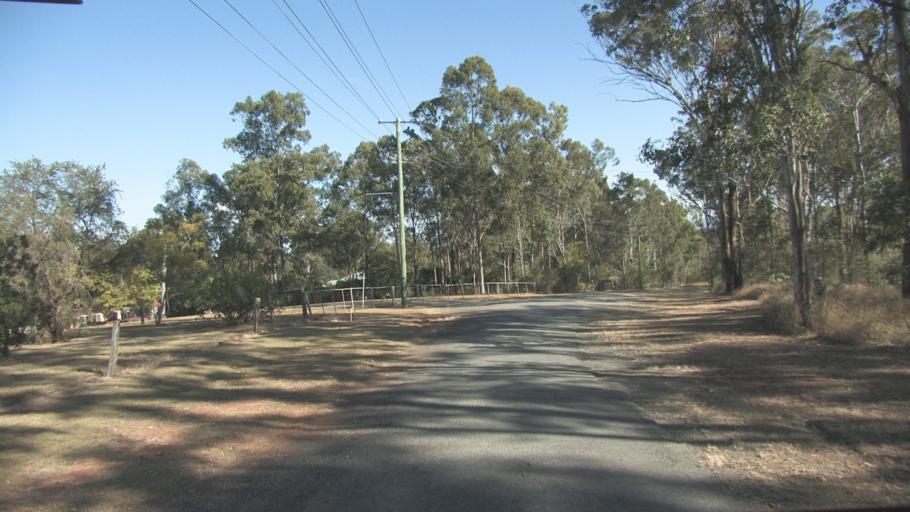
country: AU
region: Queensland
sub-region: Logan
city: Cedar Vale
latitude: -27.8622
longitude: 152.9829
